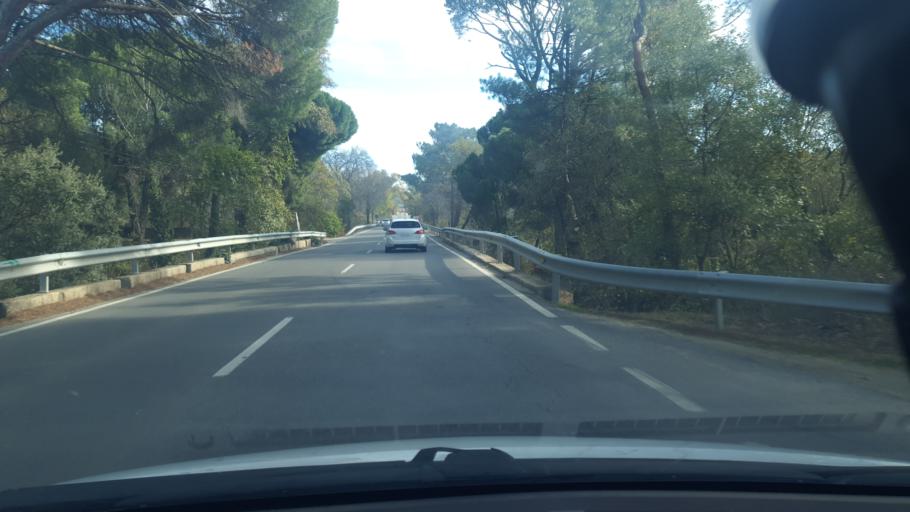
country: ES
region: Castille and Leon
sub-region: Provincia de Avila
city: La Adrada
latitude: 40.3083
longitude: -4.6520
